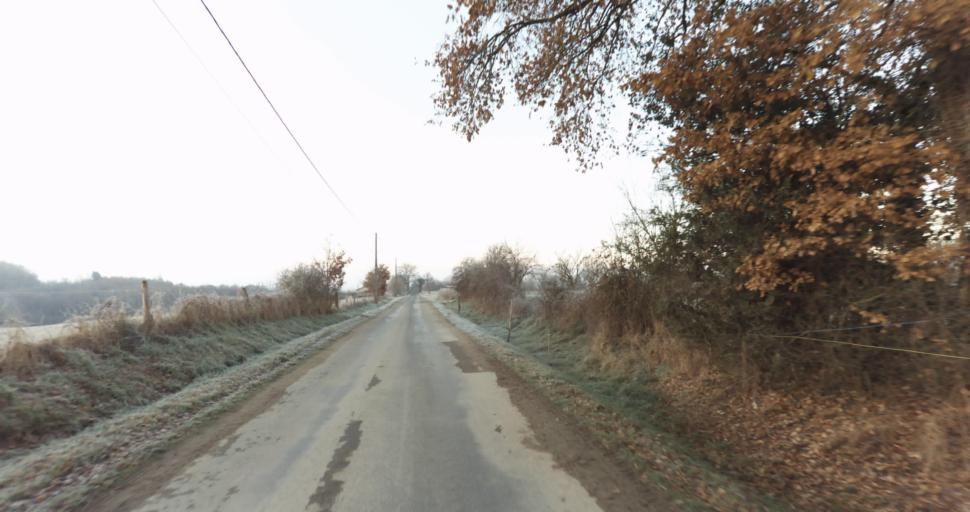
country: FR
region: Limousin
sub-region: Departement de la Haute-Vienne
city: Aixe-sur-Vienne
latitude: 45.8073
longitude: 1.1300
